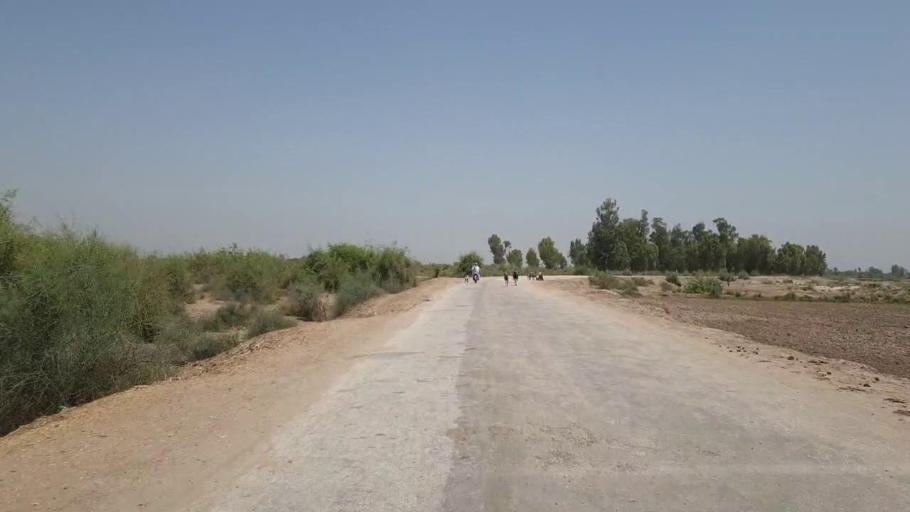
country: PK
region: Sindh
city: Adilpur
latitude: 27.8941
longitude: 69.2892
